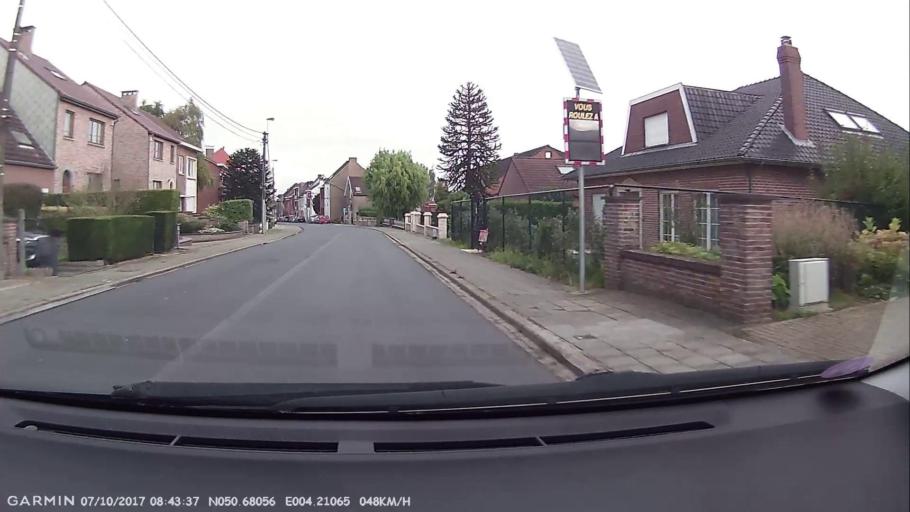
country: BE
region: Wallonia
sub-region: Province du Brabant Wallon
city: Tubize
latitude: 50.6806
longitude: 4.2106
